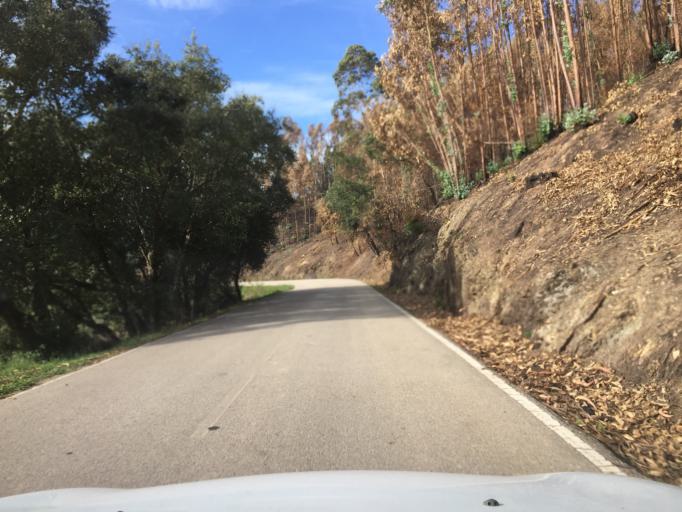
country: PT
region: Aveiro
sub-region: Mealhada
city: Mealhada
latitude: 40.3921
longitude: -8.3871
